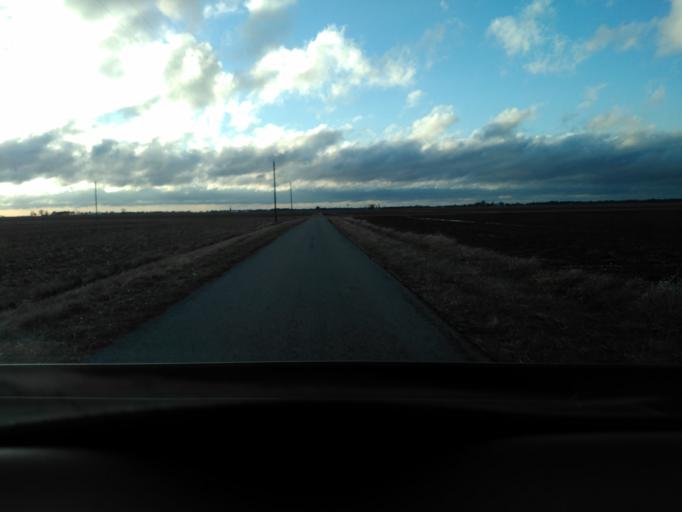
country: US
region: Illinois
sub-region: Effingham County
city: Altamont
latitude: 38.9508
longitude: -88.7100
